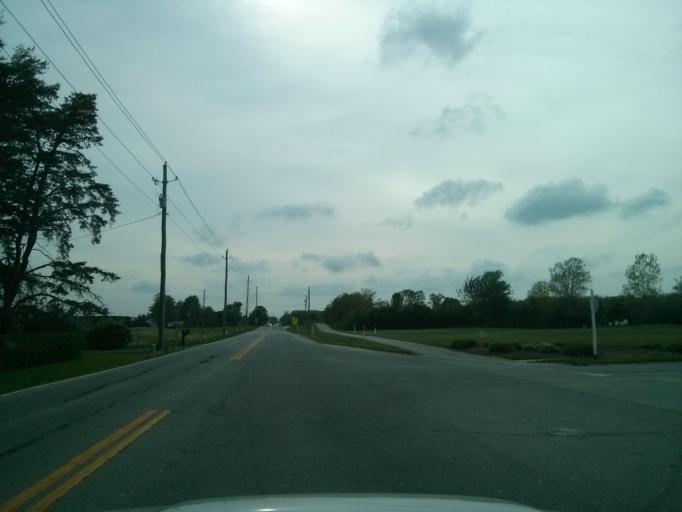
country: US
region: Indiana
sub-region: Boone County
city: Zionsville
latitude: 39.9557
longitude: -86.2058
